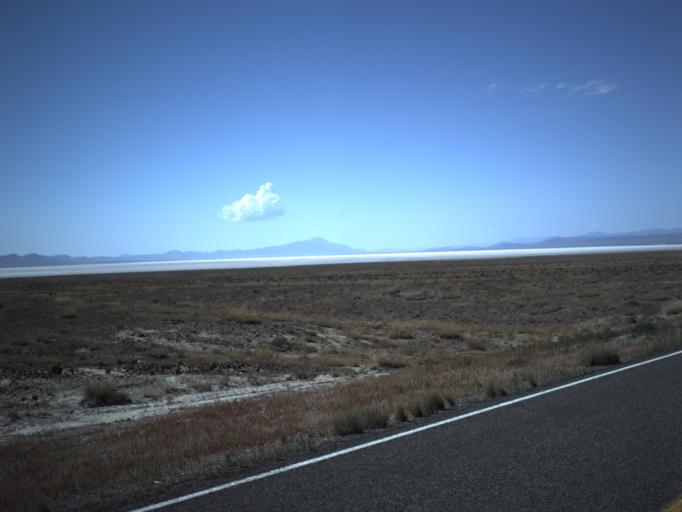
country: US
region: Utah
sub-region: Millard County
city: Delta
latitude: 39.1409
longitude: -113.0852
